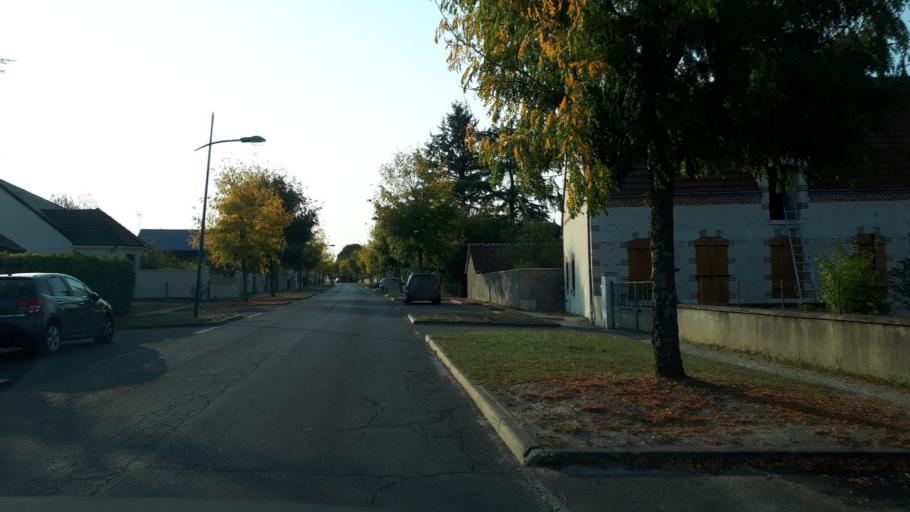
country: FR
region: Centre
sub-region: Departement du Loir-et-Cher
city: Romorantin-Lanthenay
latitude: 47.3648
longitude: 1.7285
